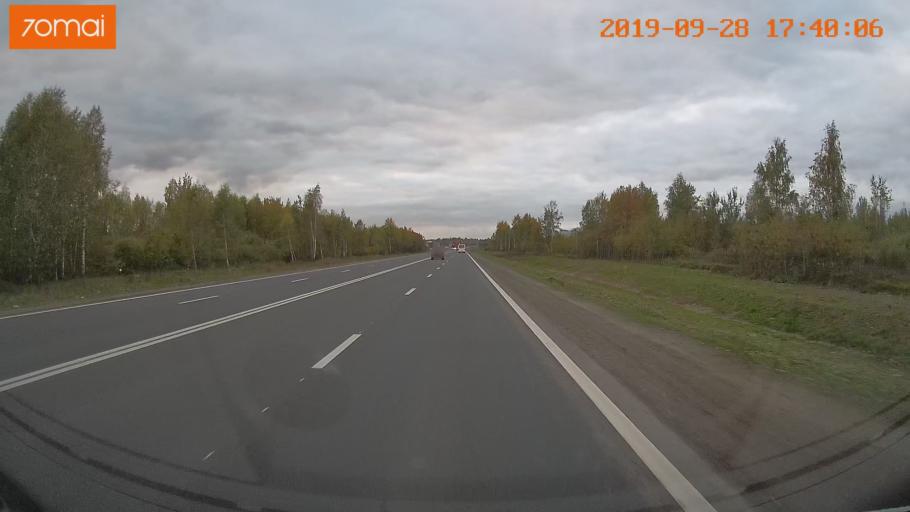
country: RU
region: Jaroslavl
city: Yaroslavl
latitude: 57.5482
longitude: 39.9028
